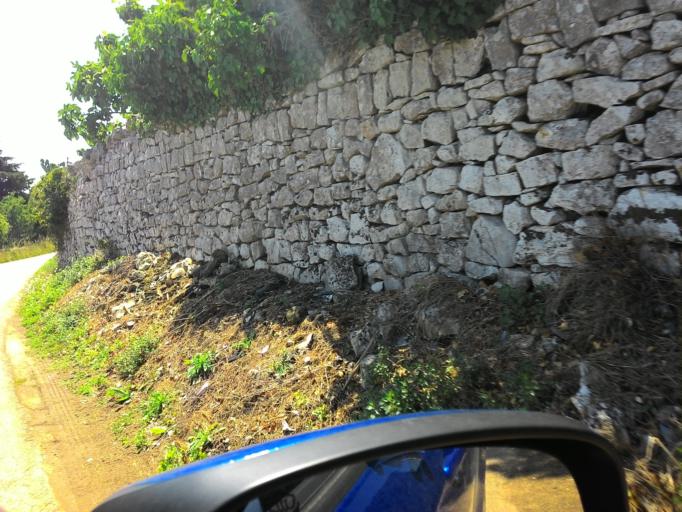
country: IT
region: Apulia
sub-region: Provincia di Bari
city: Putignano
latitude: 40.8236
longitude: 17.1368
